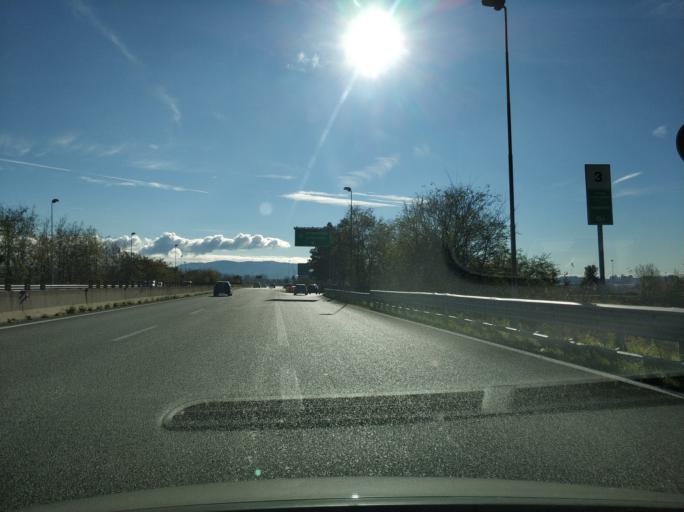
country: IT
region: Piedmont
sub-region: Provincia di Torino
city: Borgaro Torinese
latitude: 45.1286
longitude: 7.6950
